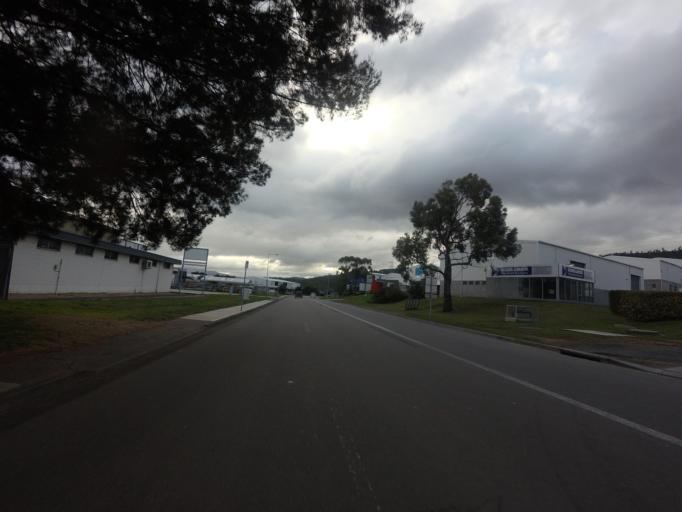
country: AU
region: Tasmania
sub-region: Clarence
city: Warrane
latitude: -42.8592
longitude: 147.3965
